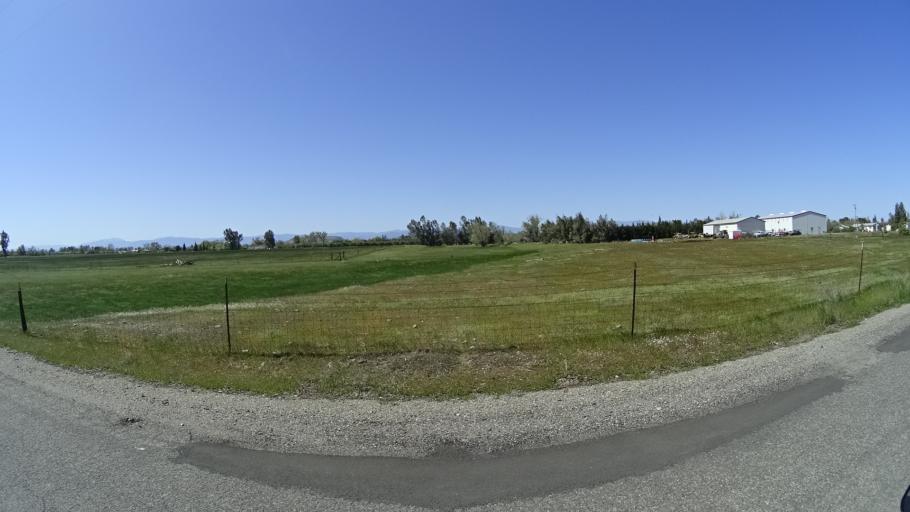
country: US
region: California
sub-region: Glenn County
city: Orland
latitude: 39.7724
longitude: -122.2293
